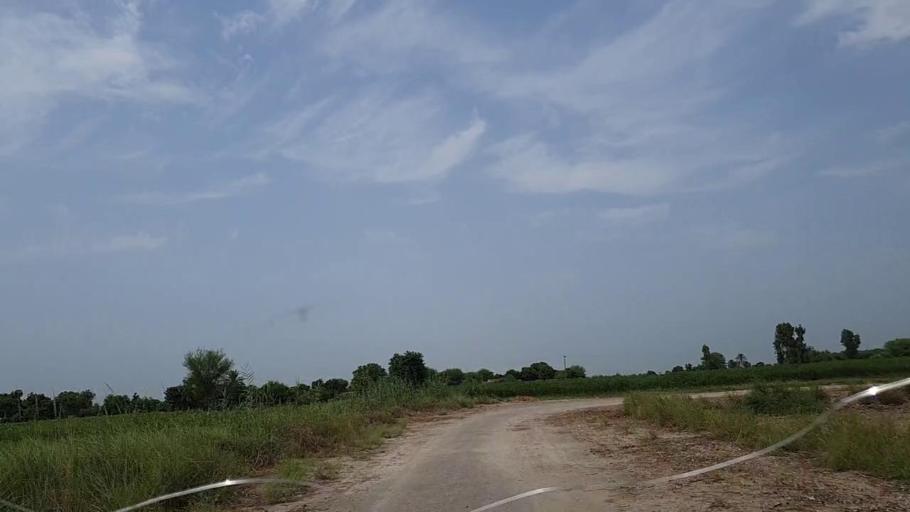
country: PK
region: Sindh
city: Tharu Shah
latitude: 26.8912
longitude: 68.0779
